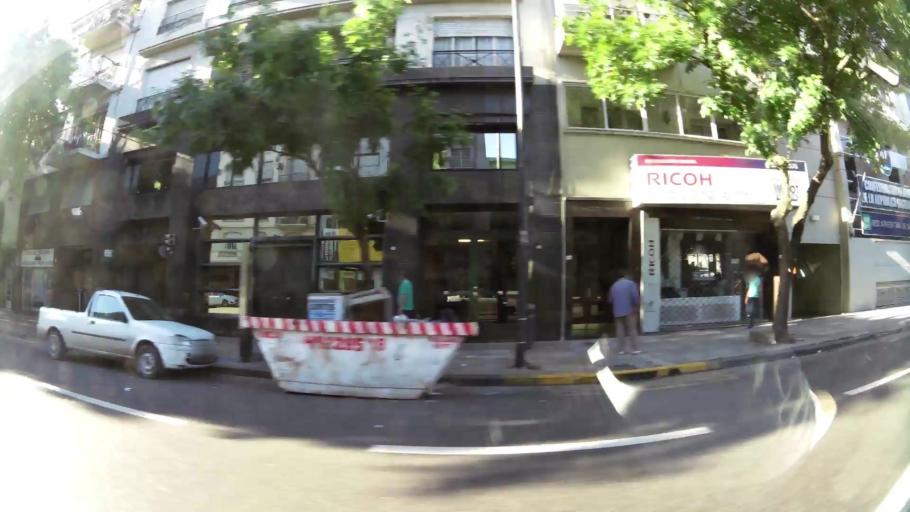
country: AR
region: Buenos Aires F.D.
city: Buenos Aires
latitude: -34.6131
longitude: -58.3840
